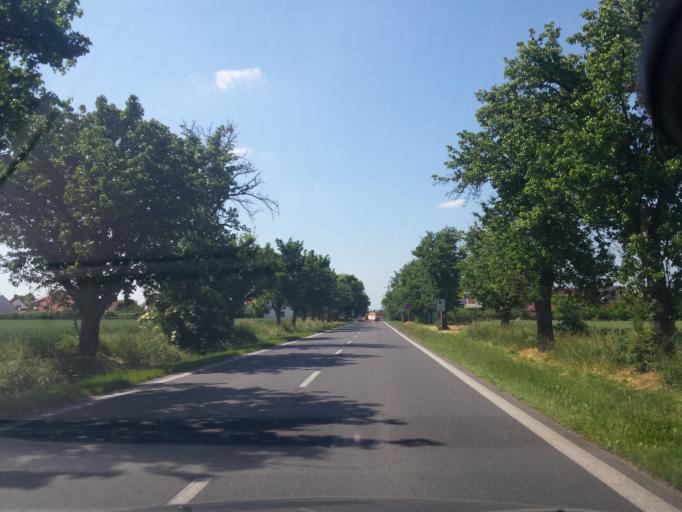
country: CZ
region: Central Bohemia
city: Horomerice
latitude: 50.1289
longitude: 14.3438
